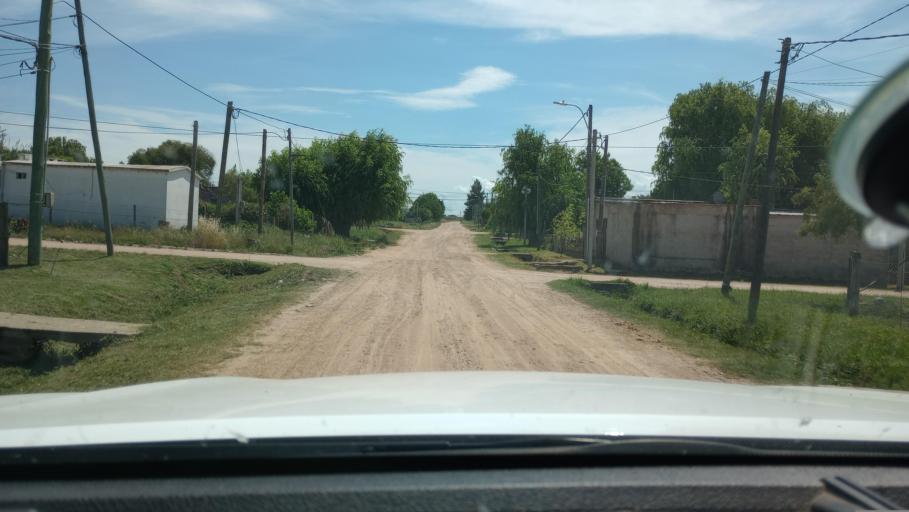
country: UY
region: Canelones
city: Joaquin Suarez
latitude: -34.7519
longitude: -56.0161
